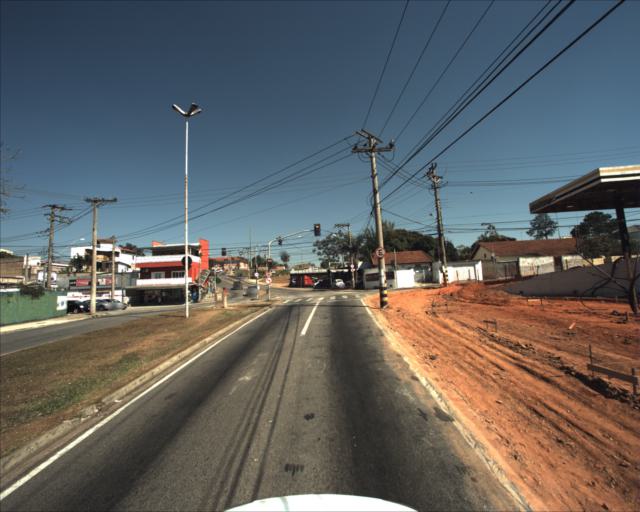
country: BR
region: Sao Paulo
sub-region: Sorocaba
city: Sorocaba
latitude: -23.5024
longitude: -47.4808
